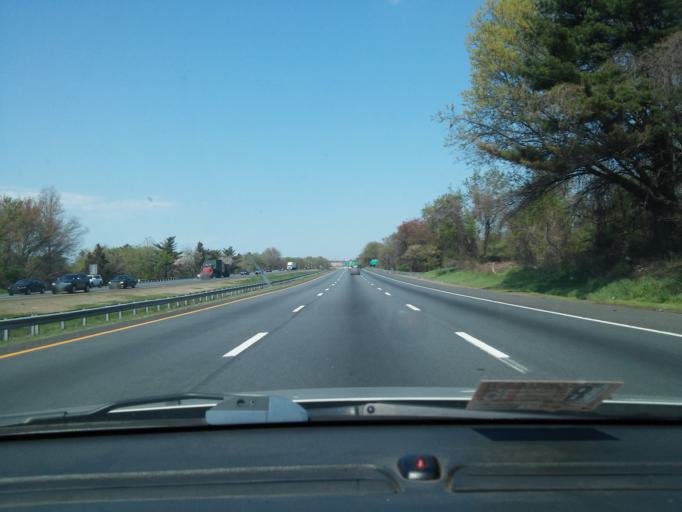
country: US
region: New Jersey
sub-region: Hunterdon County
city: Lebanon
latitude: 40.6467
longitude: -74.8206
